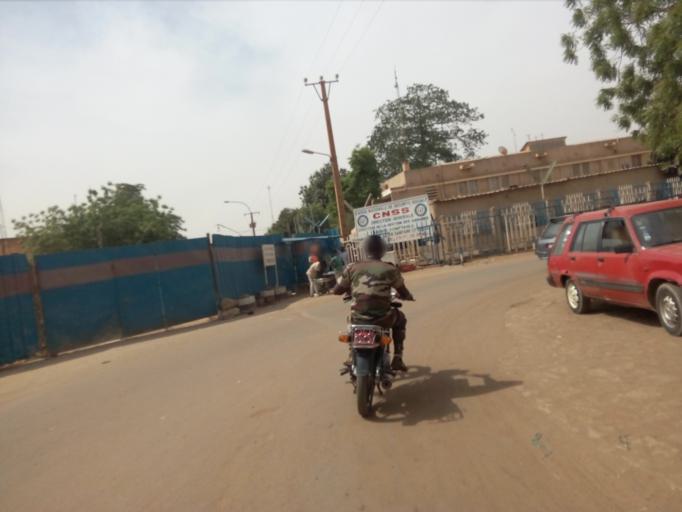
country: NE
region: Niamey
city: Niamey
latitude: 13.5171
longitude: 2.1122
